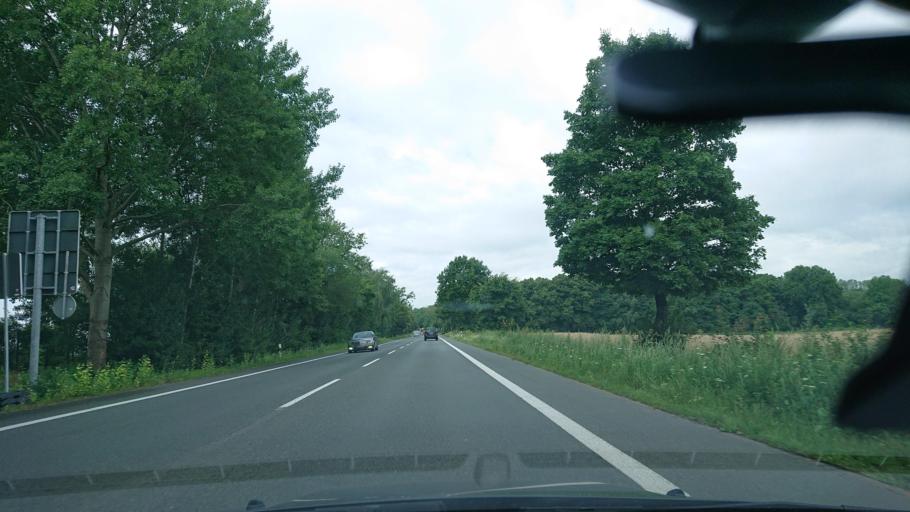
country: DE
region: North Rhine-Westphalia
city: Werne
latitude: 51.6518
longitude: 7.6695
